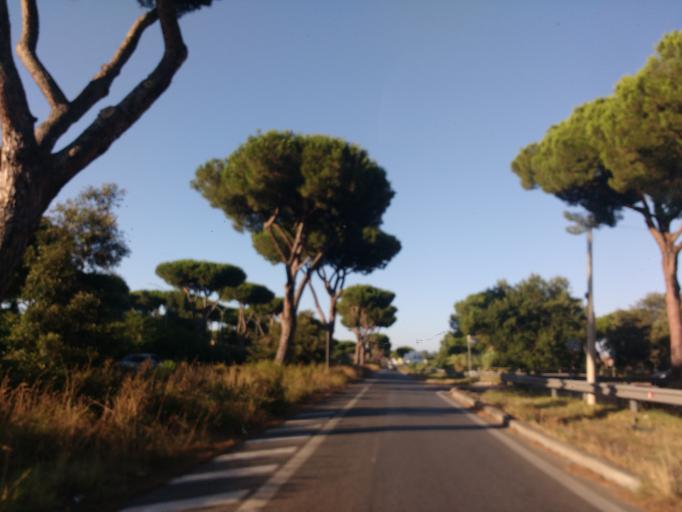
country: IT
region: Latium
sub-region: Citta metropolitana di Roma Capitale
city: Acilia-Castel Fusano-Ostia Antica
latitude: 41.7487
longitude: 12.3620
